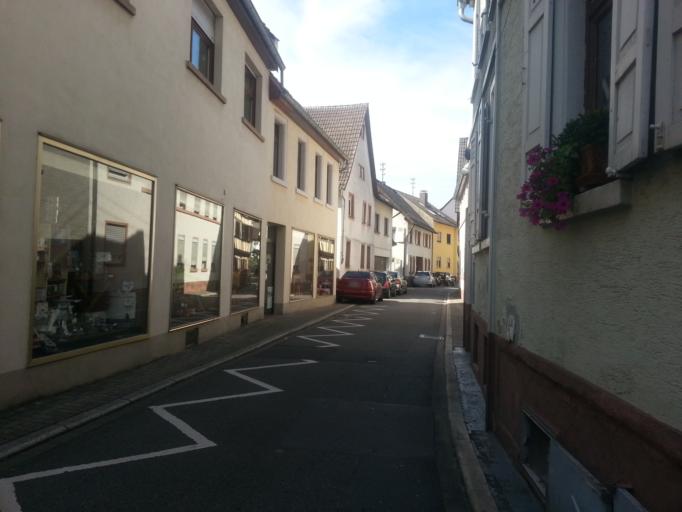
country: DE
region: Baden-Wuerttemberg
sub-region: Karlsruhe Region
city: Schriesheim
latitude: 49.4763
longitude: 8.6645
